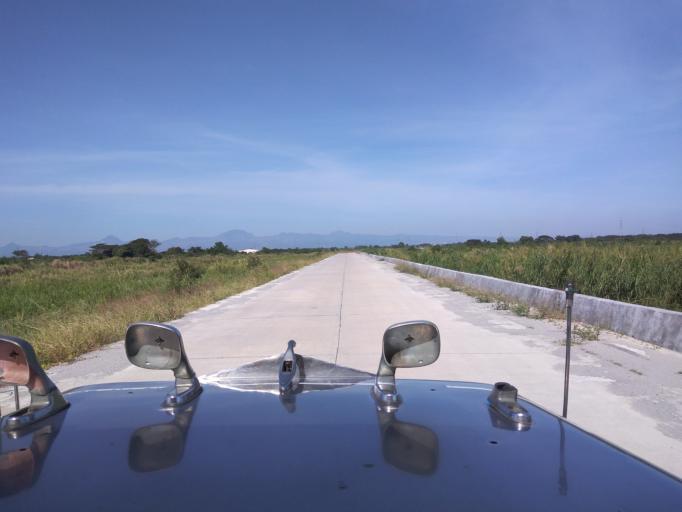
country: PH
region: Central Luzon
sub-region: Province of Pampanga
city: Bacolor
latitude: 14.9940
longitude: 120.6698
